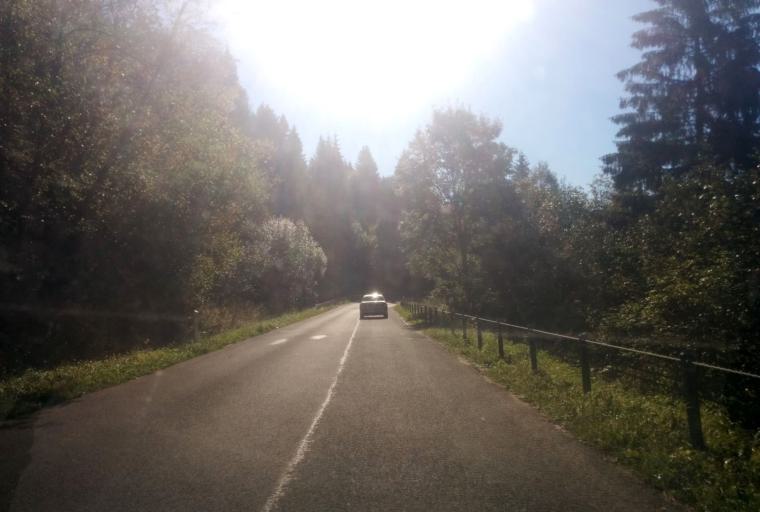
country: PL
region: Subcarpathian Voivodeship
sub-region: Powiat leski
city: Cisna
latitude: 49.2001
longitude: 22.3665
